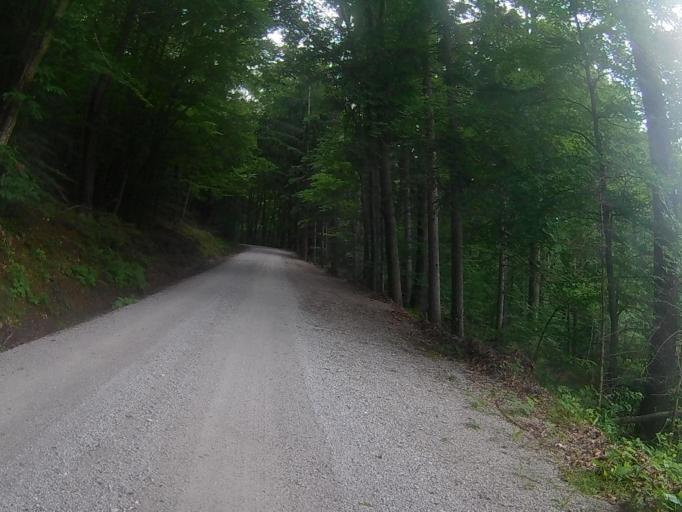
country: SI
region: Ruse
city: Bistrica ob Dravi
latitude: 46.5291
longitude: 15.5403
